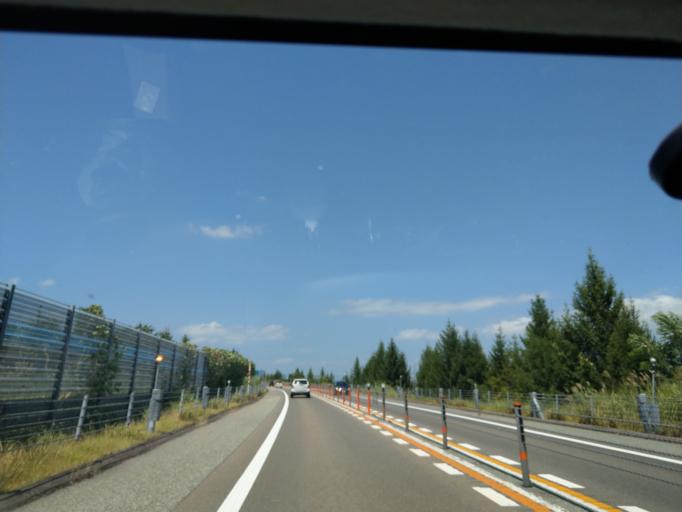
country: JP
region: Akita
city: Omagari
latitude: 39.3934
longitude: 140.4781
